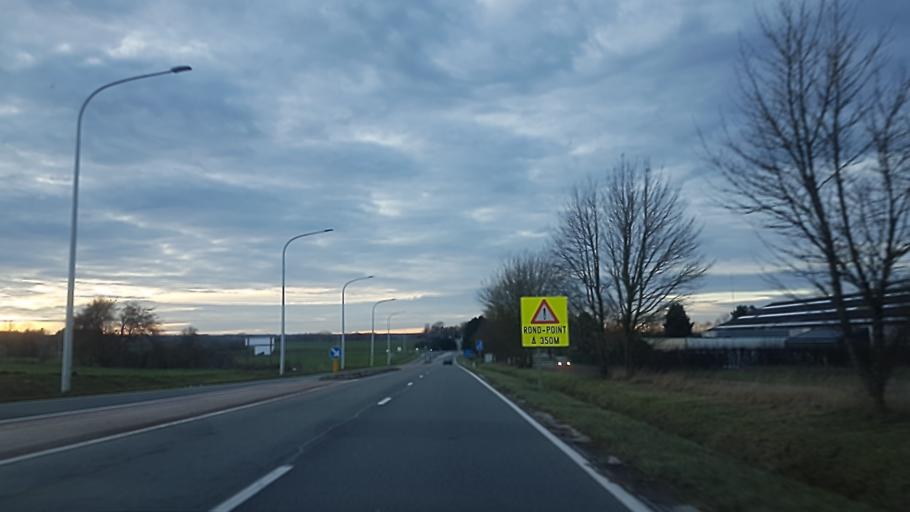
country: BE
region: Wallonia
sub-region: Province du Hainaut
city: Chimay
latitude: 50.0356
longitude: 4.3812
